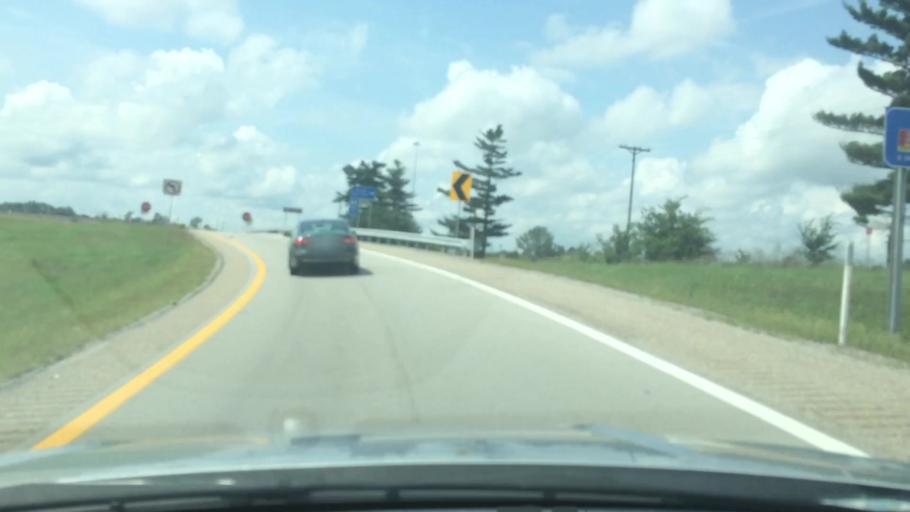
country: US
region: Kentucky
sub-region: Franklin County
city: Frankfort
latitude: 38.1600
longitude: -84.8922
